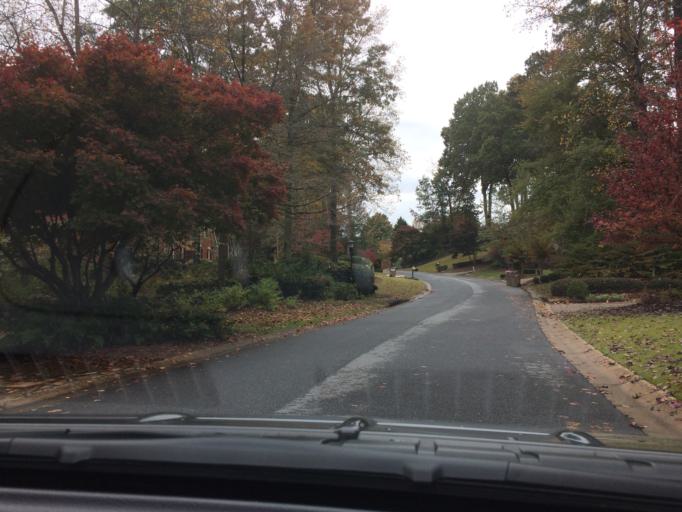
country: US
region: Georgia
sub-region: Fulton County
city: Johns Creek
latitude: 34.0105
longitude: -84.2349
